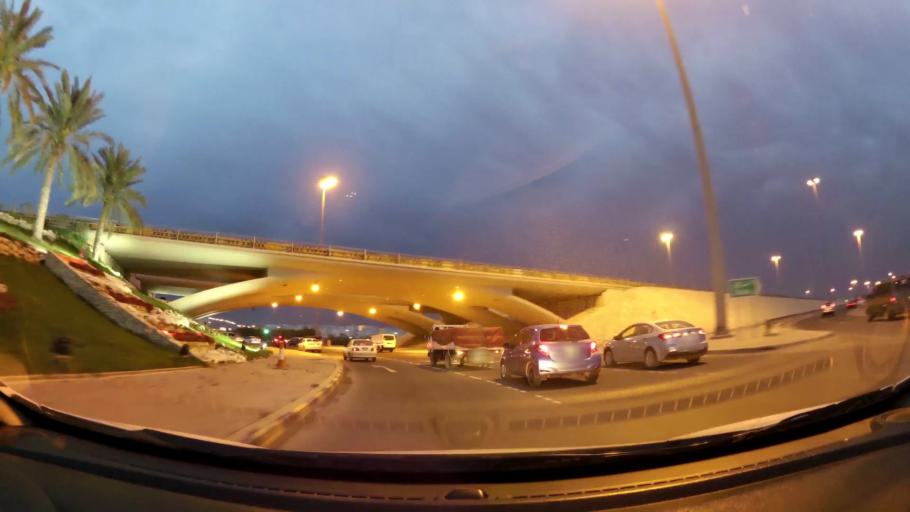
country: BH
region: Central Governorate
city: Madinat Hamad
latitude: 26.1392
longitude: 50.5102
